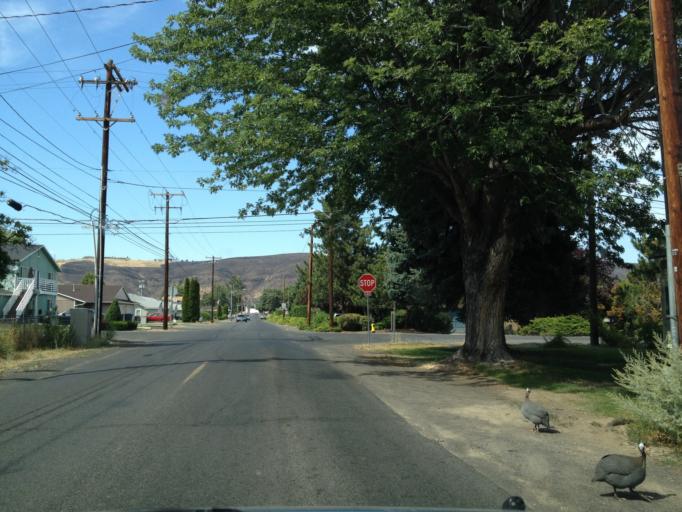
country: US
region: Washington
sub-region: Yakima County
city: Selah
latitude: 46.6121
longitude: -120.5541
